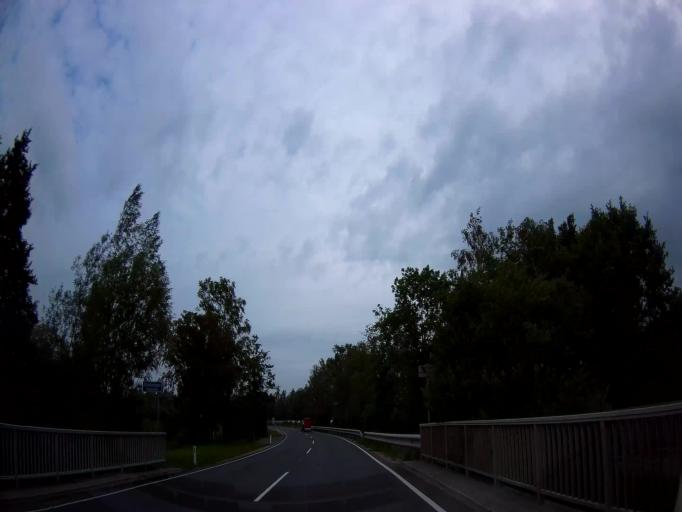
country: AT
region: Salzburg
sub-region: Politischer Bezirk Salzburg-Umgebung
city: Mattsee
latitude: 47.9781
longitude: 13.1056
